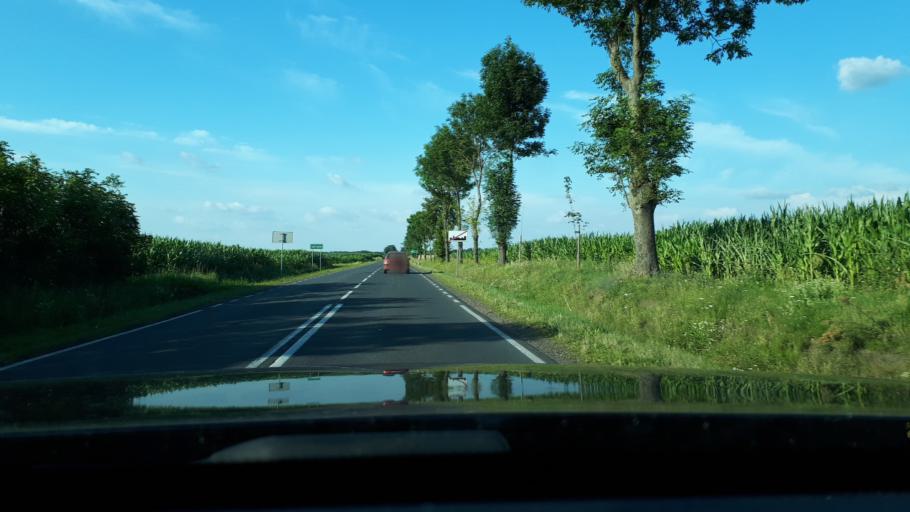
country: PL
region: Masovian Voivodeship
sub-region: Powiat plonski
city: Sochocin
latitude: 52.6931
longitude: 20.4767
